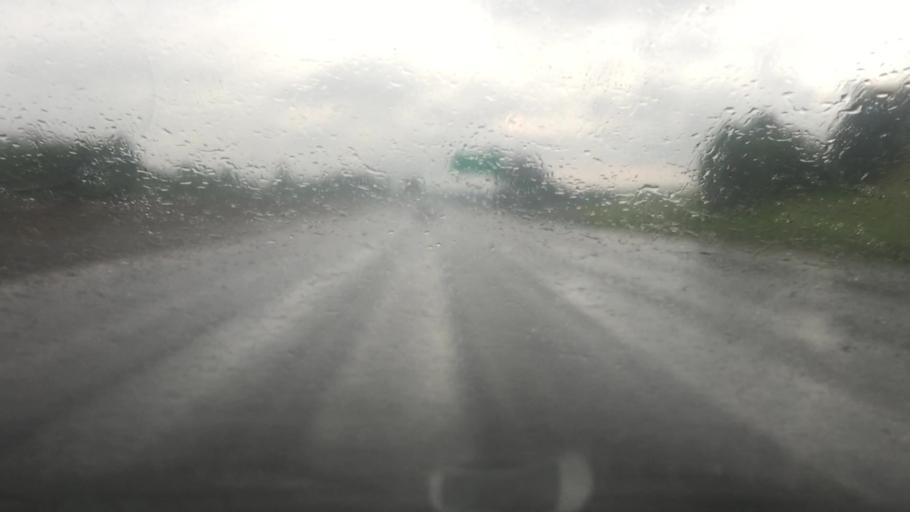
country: US
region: Missouri
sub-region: Saint Charles County
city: Weldon Spring
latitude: 38.6748
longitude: -90.6473
